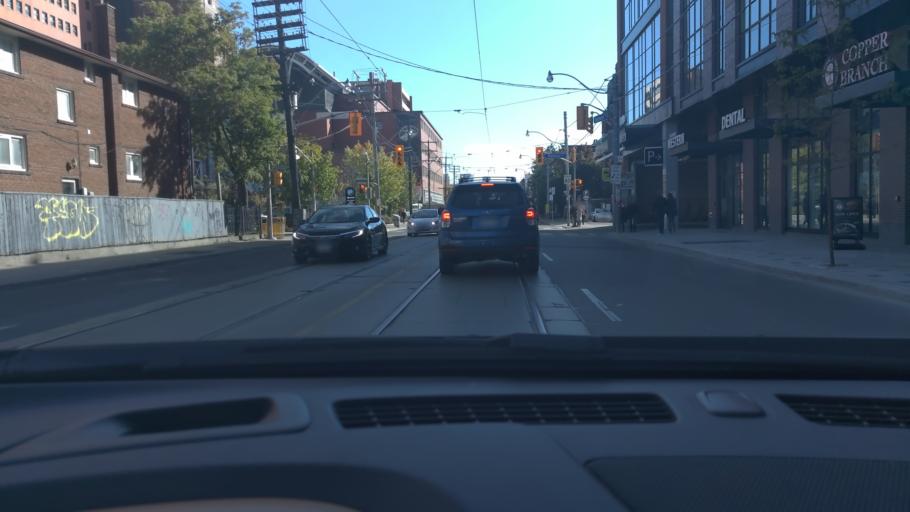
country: CA
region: Ontario
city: Toronto
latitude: 43.6547
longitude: -79.4070
